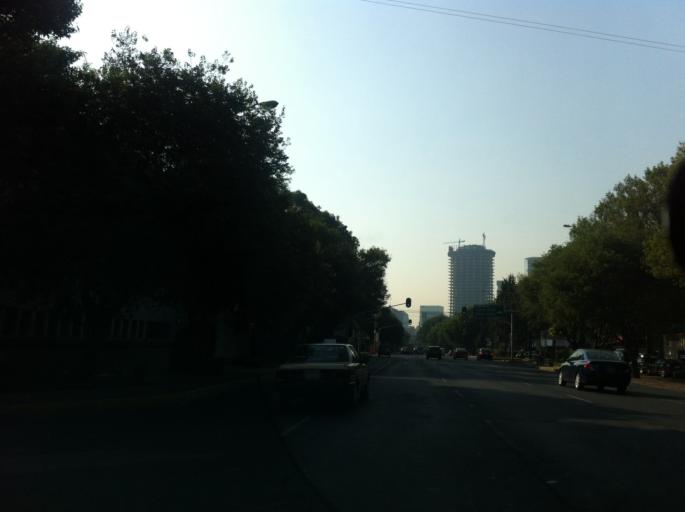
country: MX
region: Mexico City
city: Miguel Hidalgo
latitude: 19.4330
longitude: -99.1780
